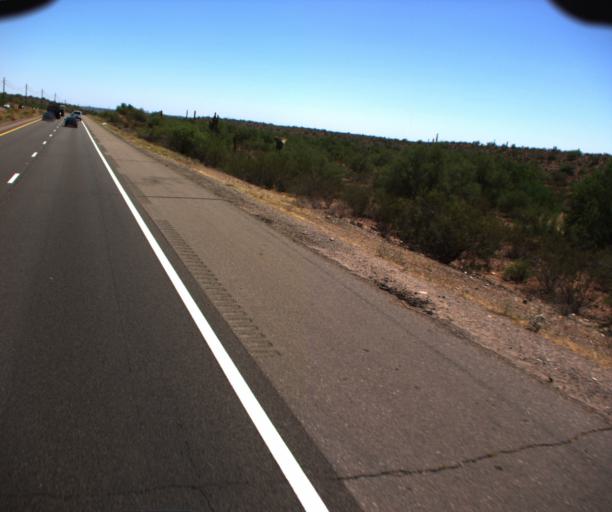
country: US
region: Arizona
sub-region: Maricopa County
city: Fountain Hills
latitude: 33.5469
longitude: -111.7232
